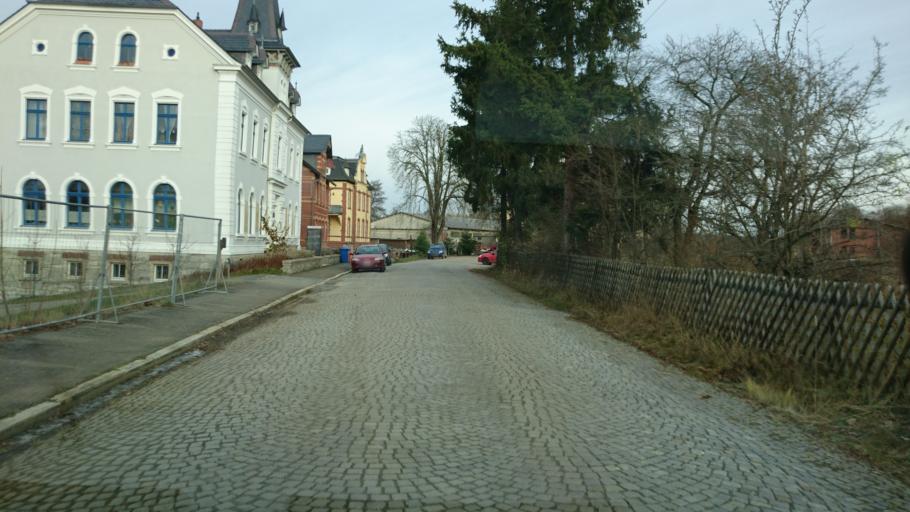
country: DE
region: Thuringia
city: Schleiz
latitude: 50.5805
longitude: 11.8161
